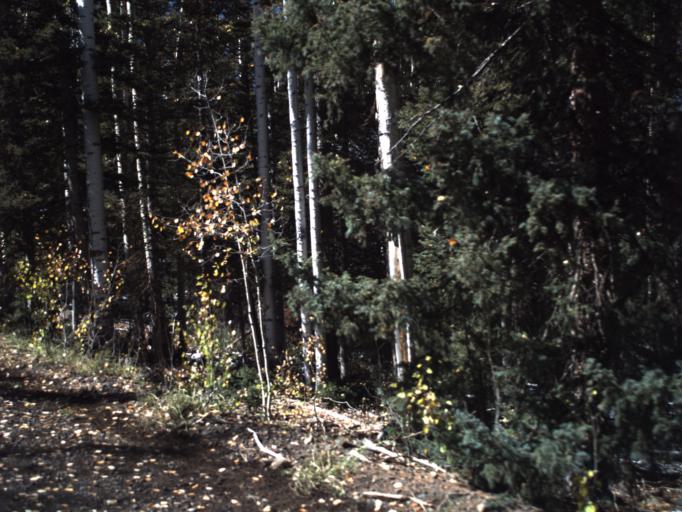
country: US
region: Utah
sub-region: Piute County
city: Junction
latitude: 38.2441
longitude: -112.3467
